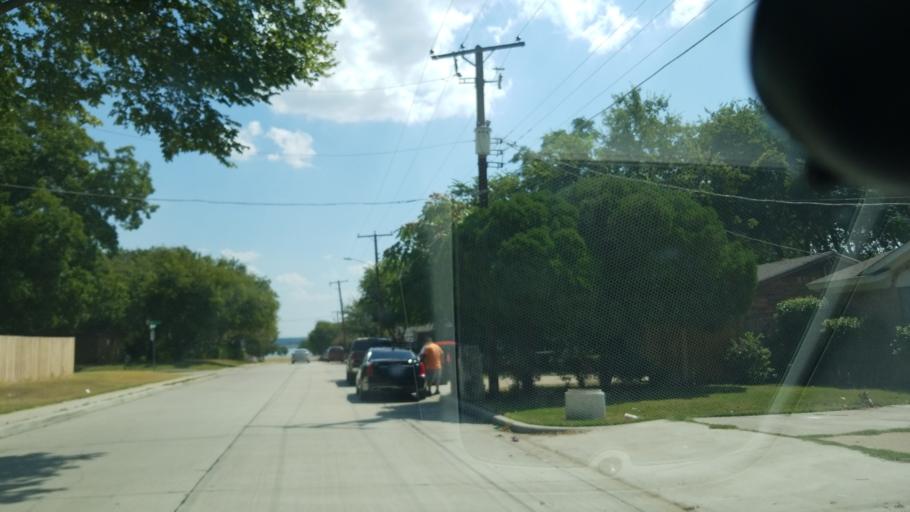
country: US
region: Texas
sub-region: Dallas County
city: Grand Prairie
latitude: 32.7104
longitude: -96.9830
